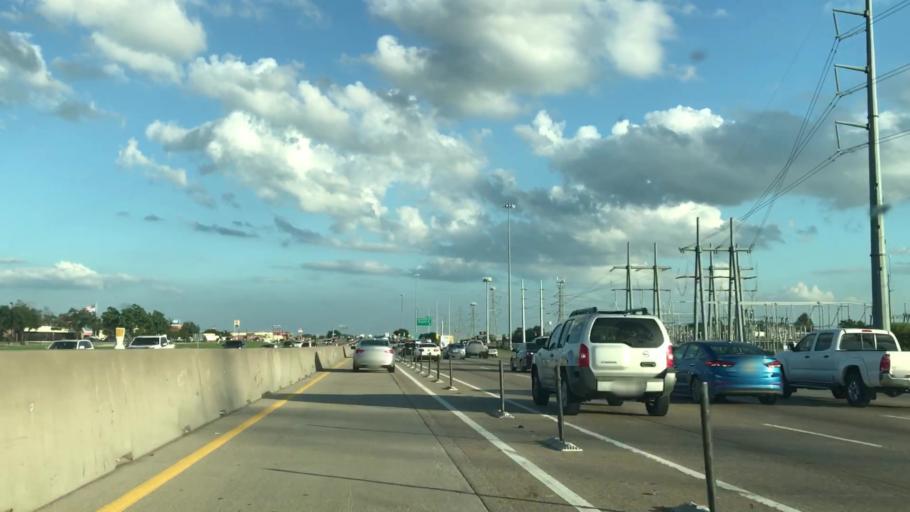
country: US
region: Texas
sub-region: Dallas County
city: Garland
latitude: 32.8598
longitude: -96.6548
